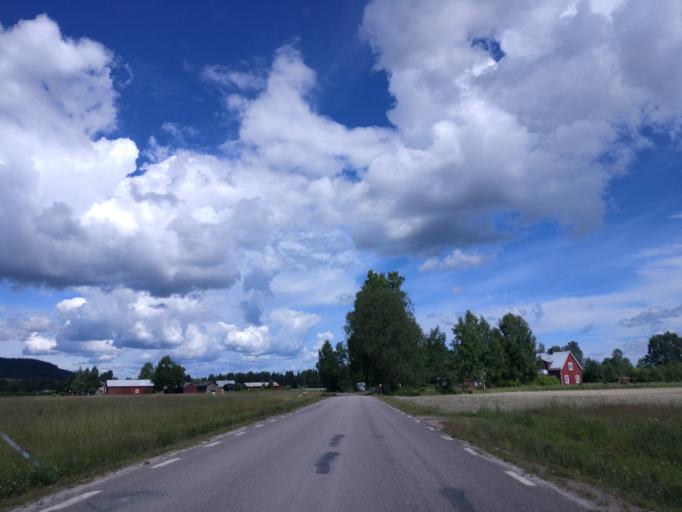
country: SE
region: Vaermland
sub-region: Hagfors Kommun
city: Ekshaerad
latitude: 60.0441
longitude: 13.4931
